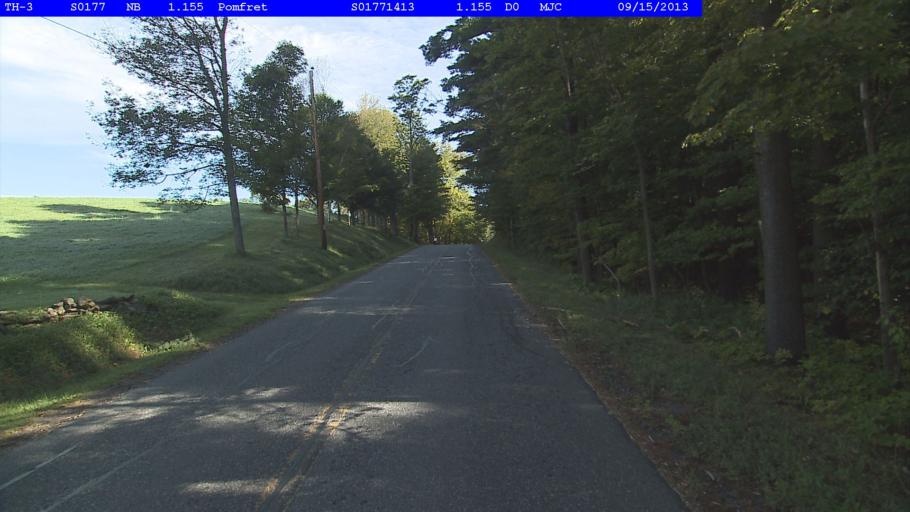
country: US
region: Vermont
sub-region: Windsor County
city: Woodstock
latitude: 43.7384
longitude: -72.4968
